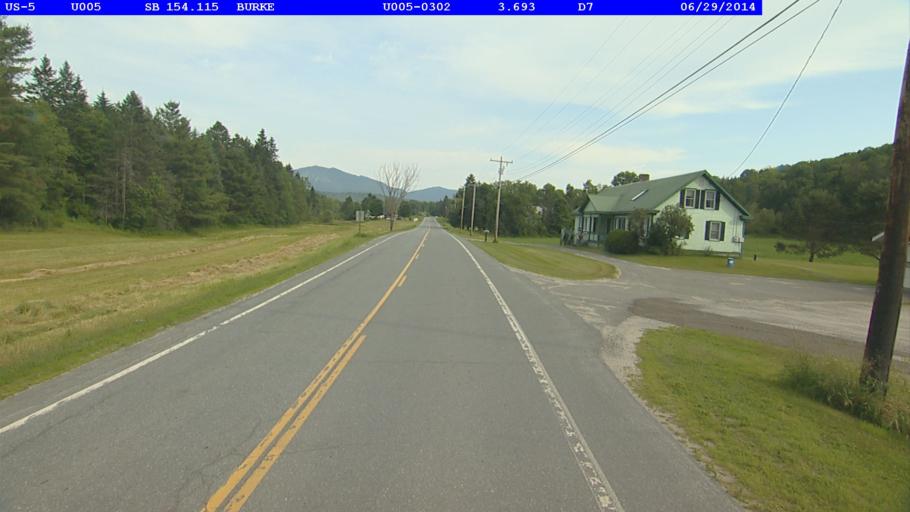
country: US
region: Vermont
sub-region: Caledonia County
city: Lyndonville
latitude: 44.6364
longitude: -71.9775
